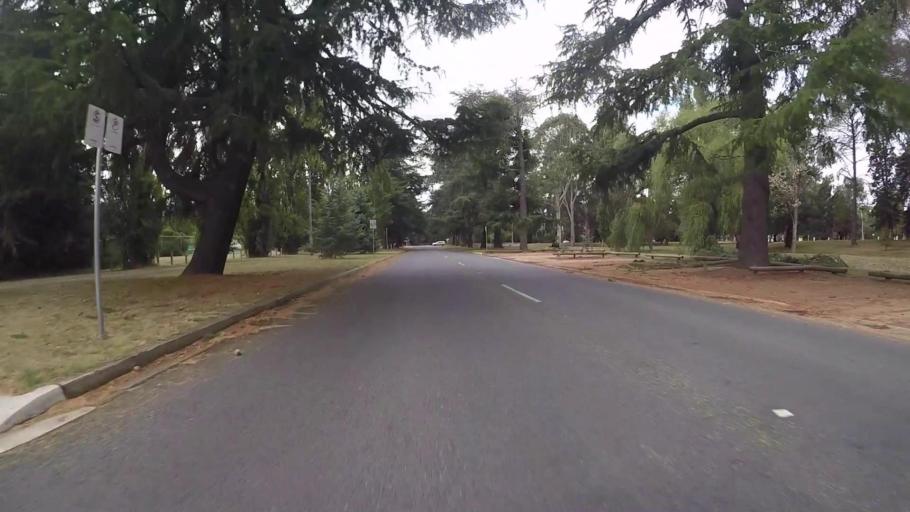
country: AU
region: Australian Capital Territory
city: Forrest
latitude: -35.3116
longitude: 149.1395
